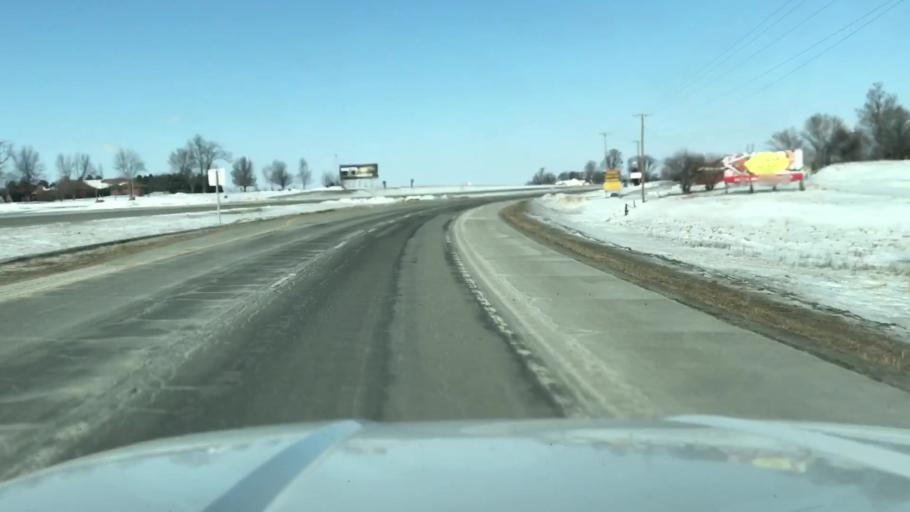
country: US
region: Missouri
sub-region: Nodaway County
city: Maryville
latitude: 40.2773
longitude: -94.8740
